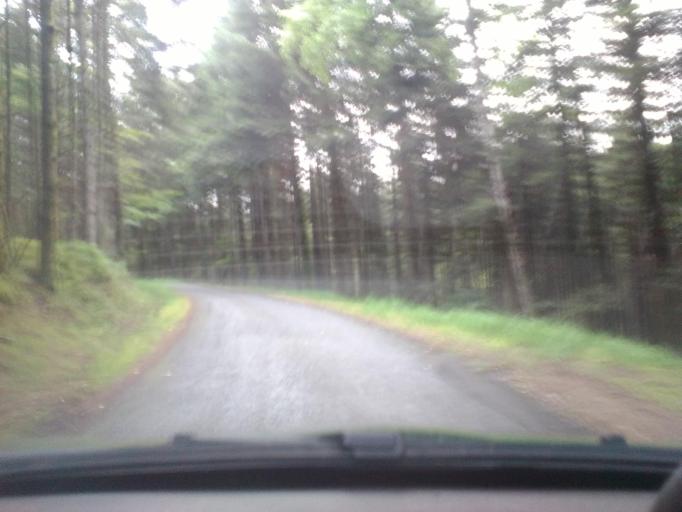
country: FR
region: Lorraine
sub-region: Departement des Vosges
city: Granges-sur-Vologne
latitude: 48.2264
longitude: 6.8117
